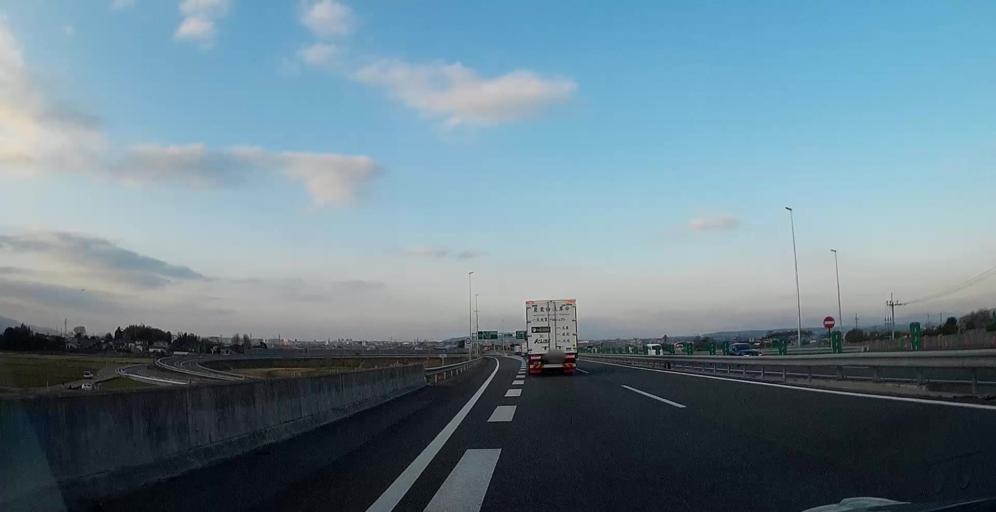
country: JP
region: Kumamoto
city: Kumamoto
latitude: 32.7534
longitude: 130.7887
